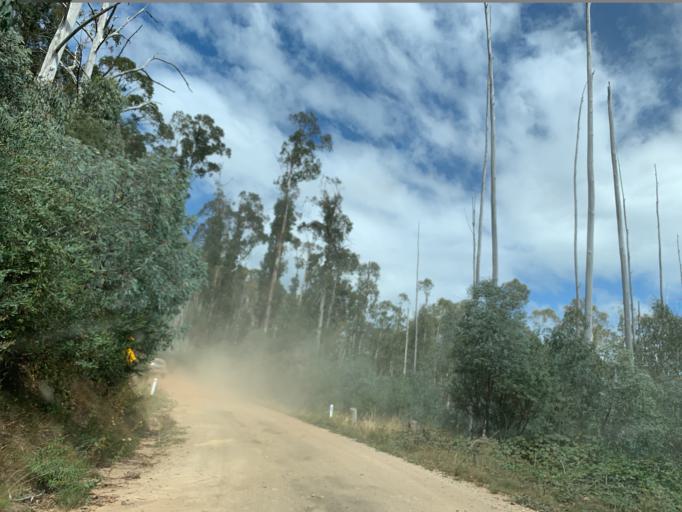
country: AU
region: Victoria
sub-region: Mansfield
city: Mansfield
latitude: -37.0972
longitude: 146.5334
